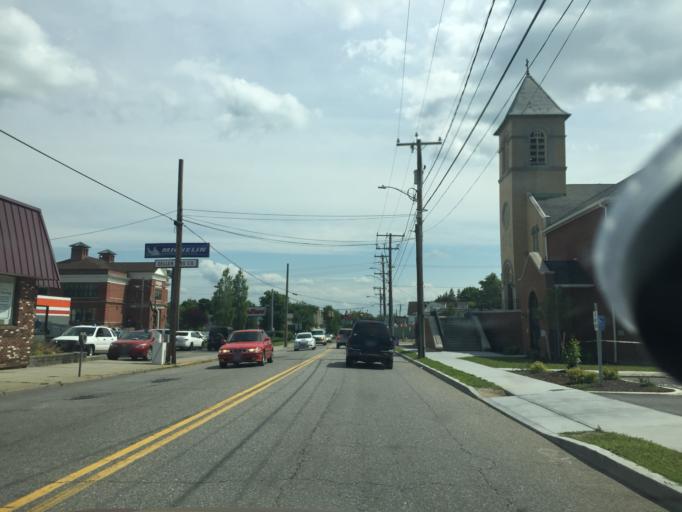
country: US
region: Connecticut
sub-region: Litchfield County
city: Torrington
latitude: 41.8132
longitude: -73.1214
